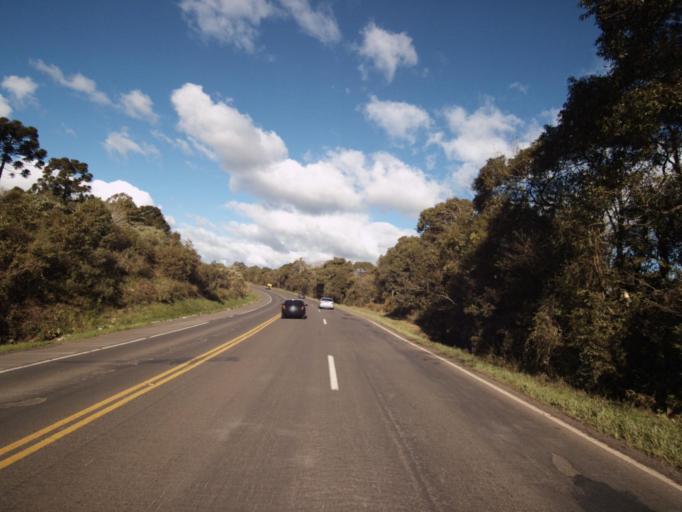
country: BR
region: Santa Catarina
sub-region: Joacaba
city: Joacaba
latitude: -27.1637
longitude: -51.5683
